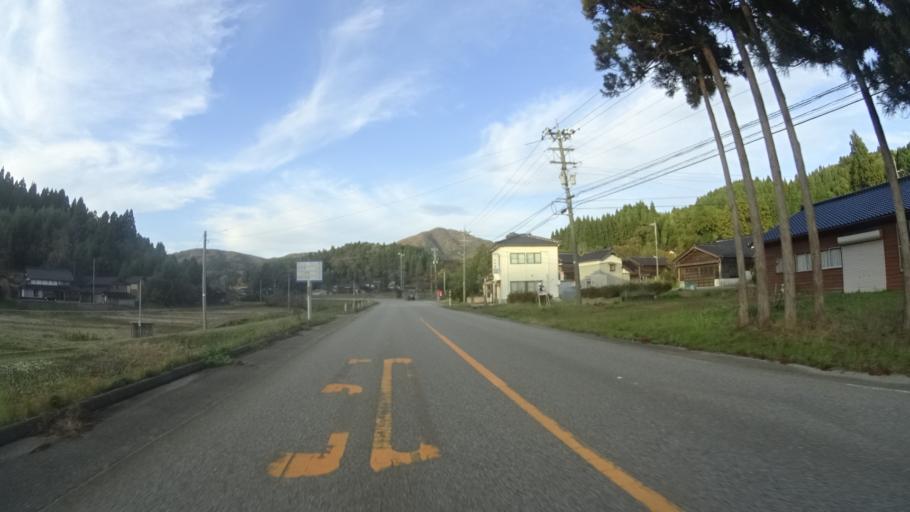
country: JP
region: Ishikawa
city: Nanao
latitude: 37.1905
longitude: 136.7167
